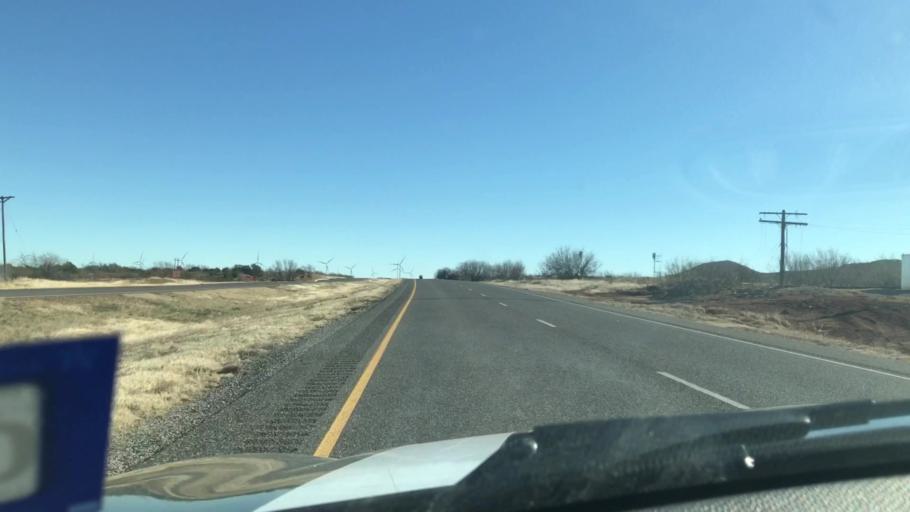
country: US
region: Texas
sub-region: Scurry County
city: Snyder
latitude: 32.9383
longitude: -101.0749
